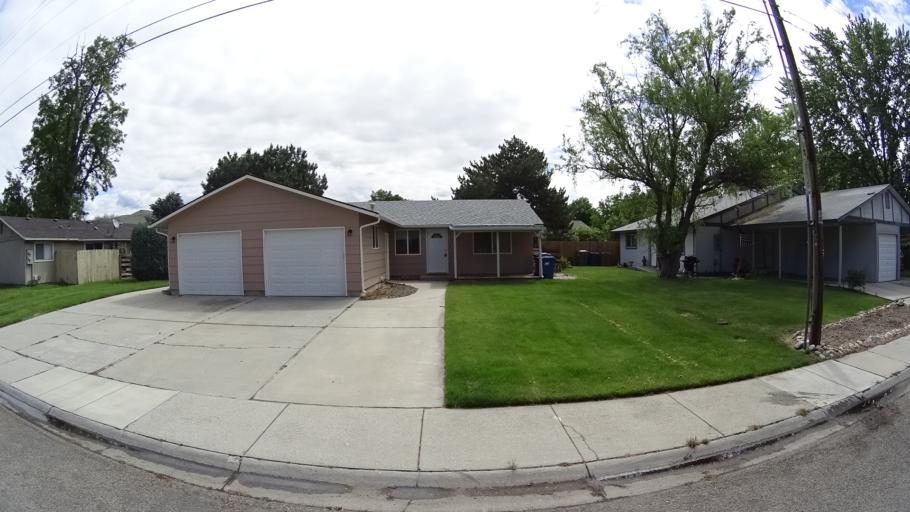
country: US
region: Idaho
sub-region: Ada County
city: Boise
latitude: 43.5725
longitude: -116.1634
